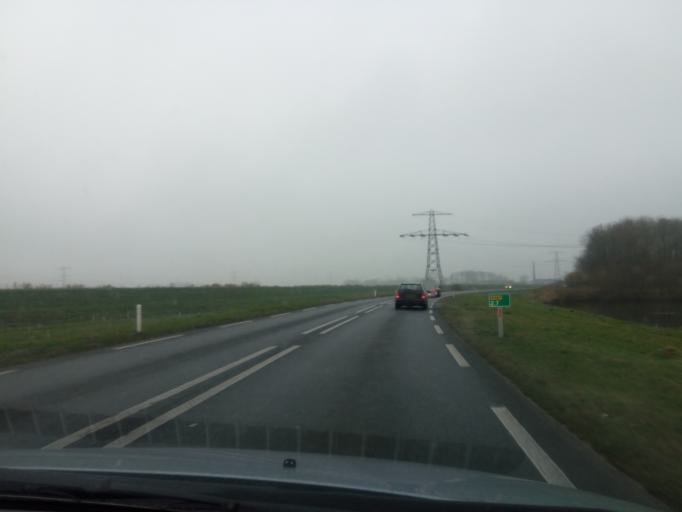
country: NL
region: Groningen
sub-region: Gemeente  Oldambt
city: Winschoten
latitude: 53.1360
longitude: 7.0623
